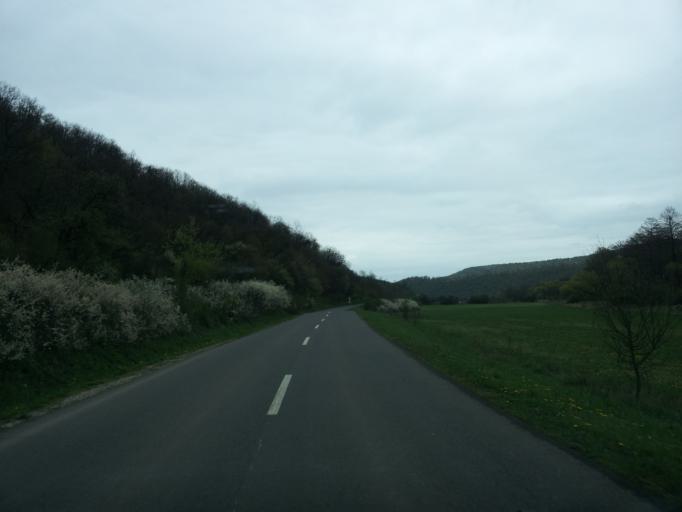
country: HU
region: Borsod-Abauj-Zemplen
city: Rudabanya
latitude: 48.4914
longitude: 20.6343
